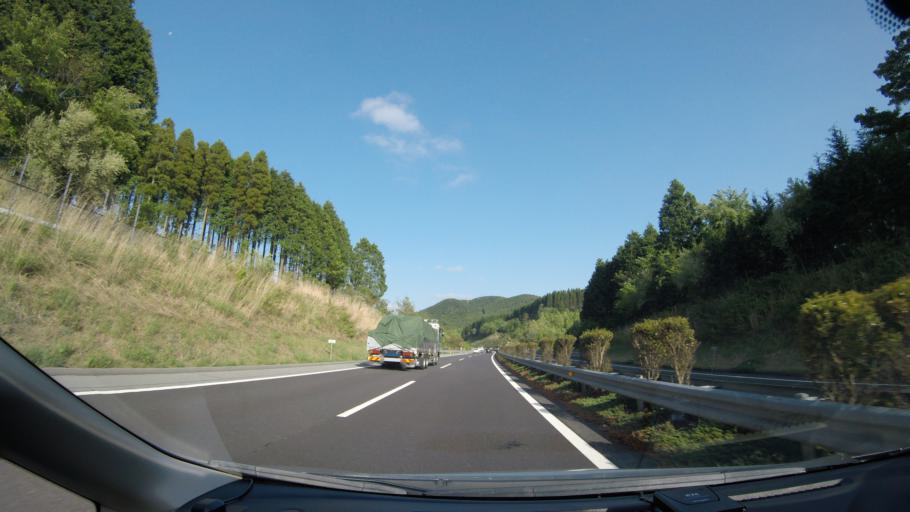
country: JP
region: Oita
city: Tsukawaki
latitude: 33.2537
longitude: 131.2732
